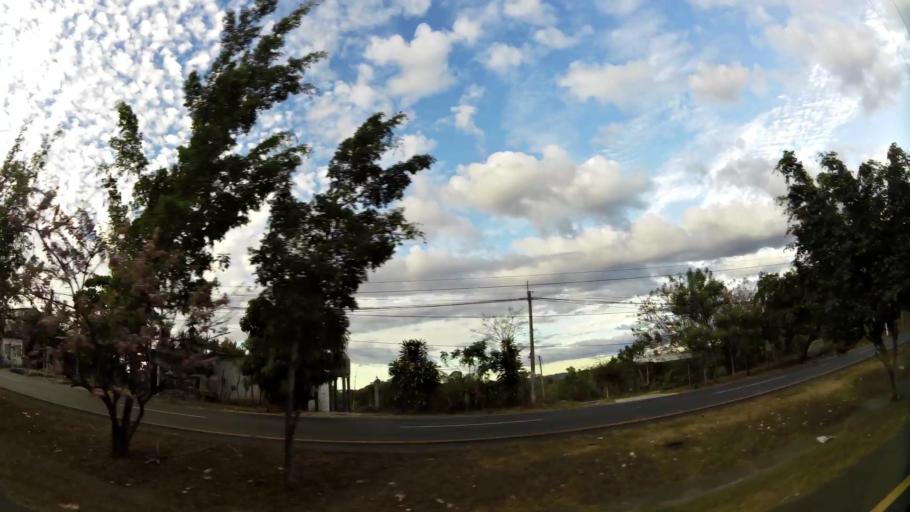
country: SV
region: Cuscatlan
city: Cojutepeque
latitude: 13.7300
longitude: -88.8933
